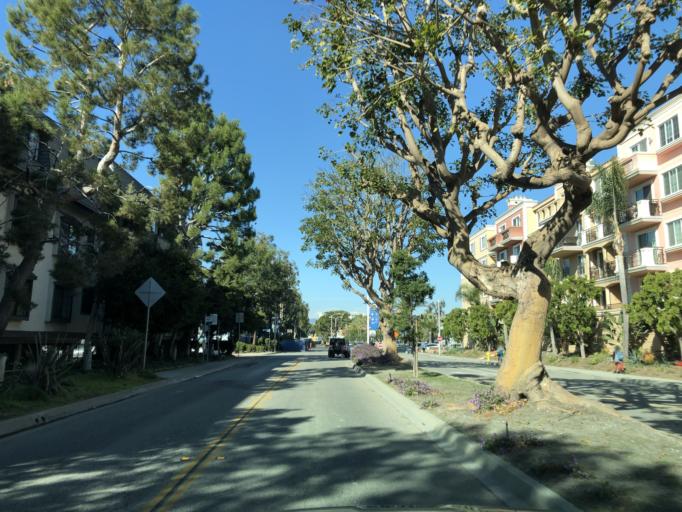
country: US
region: California
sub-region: Los Angeles County
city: Marina del Rey
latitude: 33.9706
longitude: -118.4552
